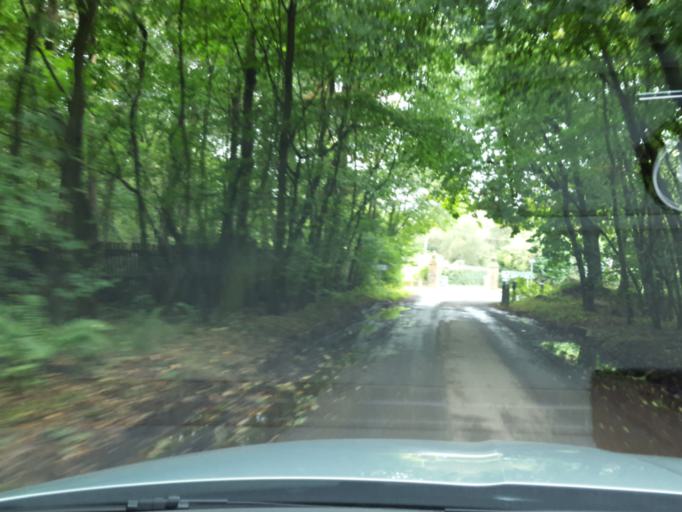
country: GB
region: Scotland
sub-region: West Lothian
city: East Calder
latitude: 55.9120
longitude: -3.4554
